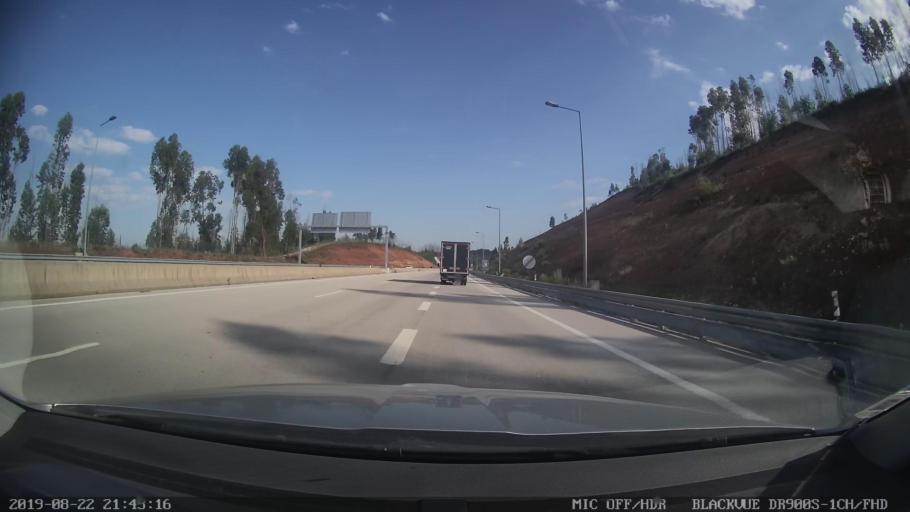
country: PT
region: Leiria
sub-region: Figueiro Dos Vinhos
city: Figueiro dos Vinhos
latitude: 39.9303
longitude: -8.3458
